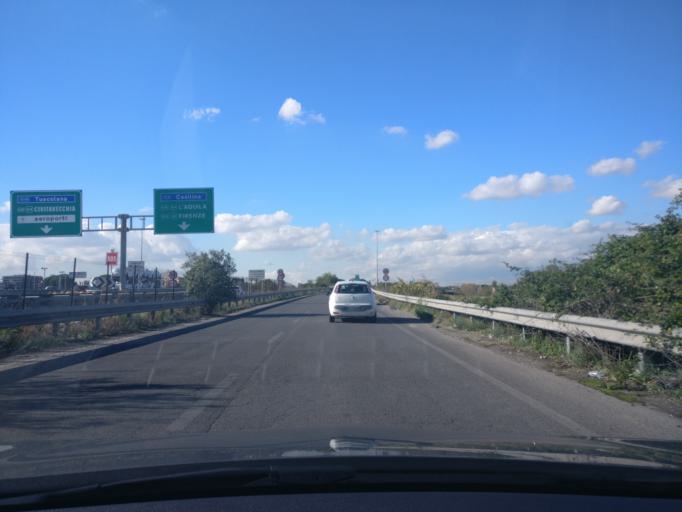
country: IT
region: Latium
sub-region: Citta metropolitana di Roma Capitale
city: Ciampino
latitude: 41.8517
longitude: 12.6023
